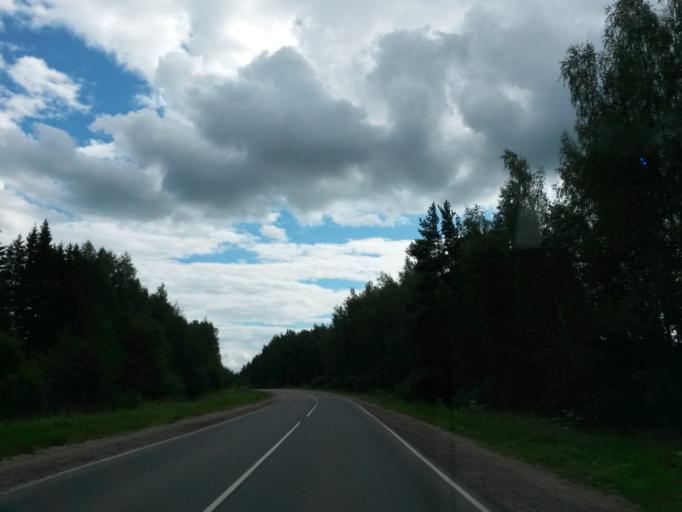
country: RU
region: Ivanovo
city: Pistsovo
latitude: 57.0925
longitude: 40.6622
